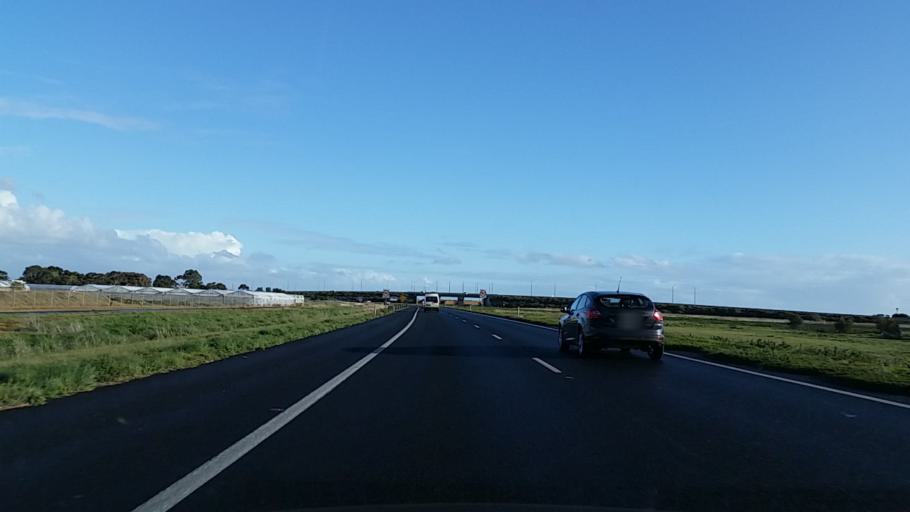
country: AU
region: South Australia
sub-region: Playford
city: Virginia
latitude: -34.7004
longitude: 138.5760
